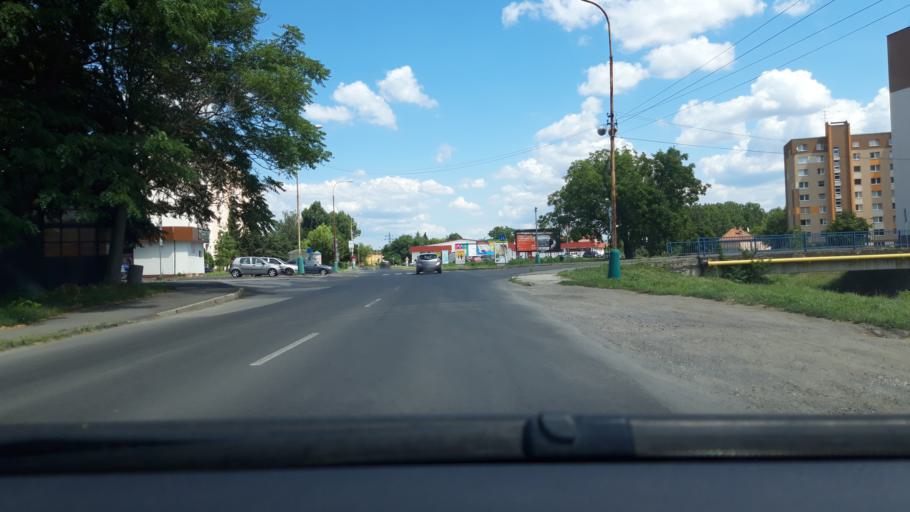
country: SK
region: Banskobystricky
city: Lucenec
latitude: 48.3254
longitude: 19.6738
